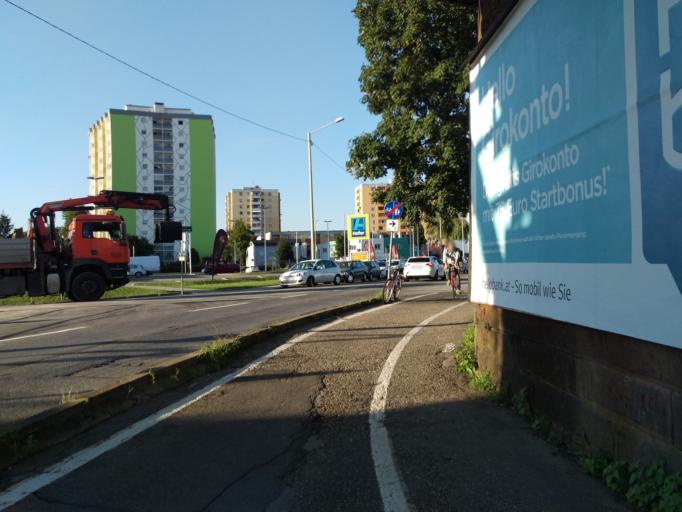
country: AT
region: Styria
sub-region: Graz Stadt
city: Graz
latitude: 47.0559
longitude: 15.4285
